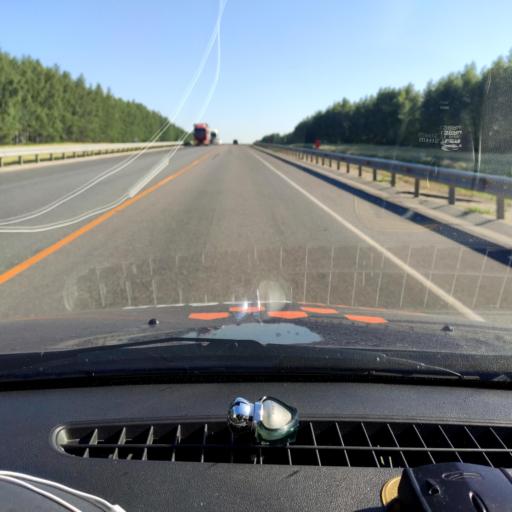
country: RU
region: Orjol
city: Zmiyevka
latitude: 52.7615
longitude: 36.3208
